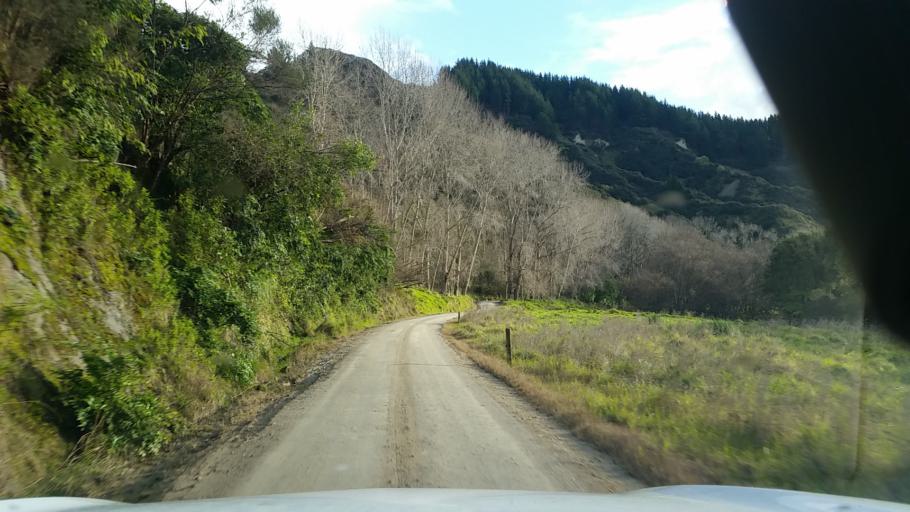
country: NZ
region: Taranaki
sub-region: South Taranaki District
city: Patea
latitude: -39.5722
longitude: 174.8172
